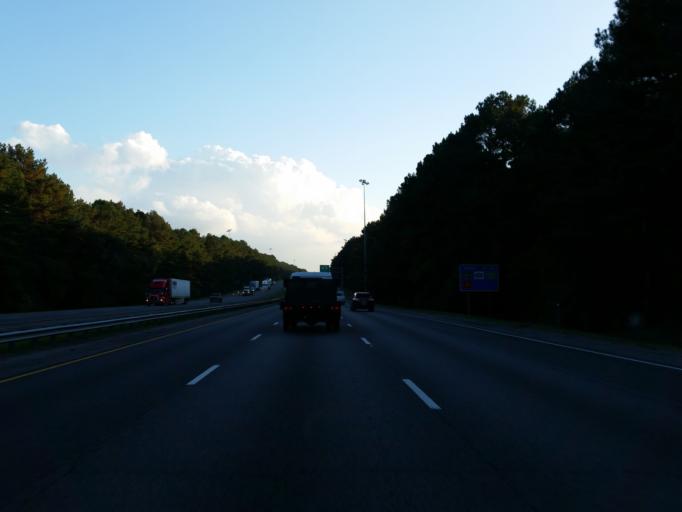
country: US
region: Georgia
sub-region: Houston County
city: Perry
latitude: 32.4879
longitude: -83.7426
